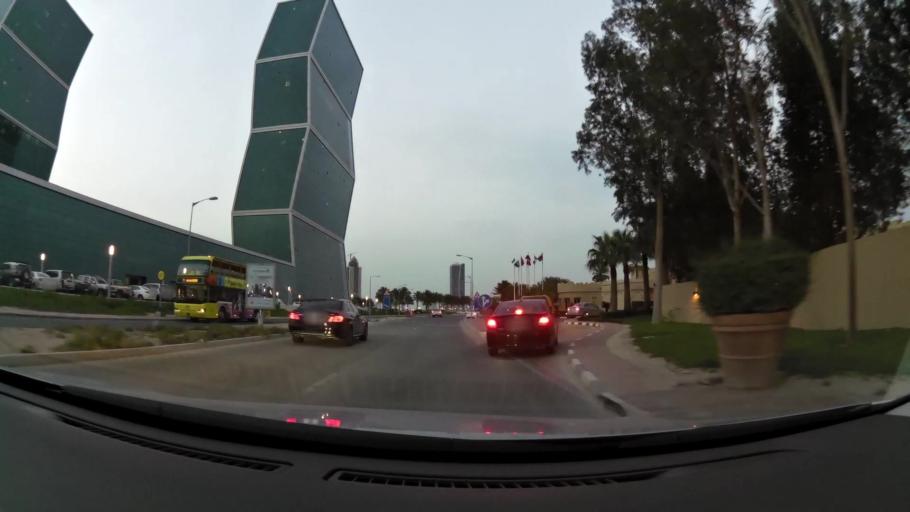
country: QA
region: Baladiyat ad Dawhah
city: Doha
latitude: 25.3762
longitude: 51.5261
